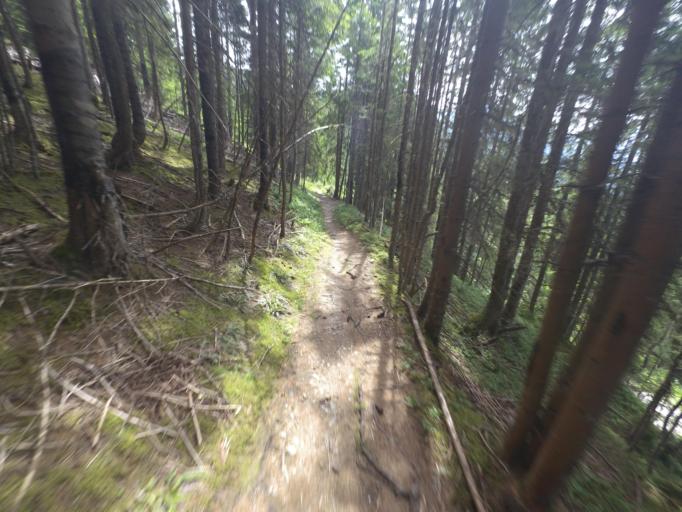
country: AT
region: Salzburg
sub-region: Politischer Bezirk Sankt Johann im Pongau
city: Muhlbach am Hochkonig
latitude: 47.3633
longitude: 13.1063
